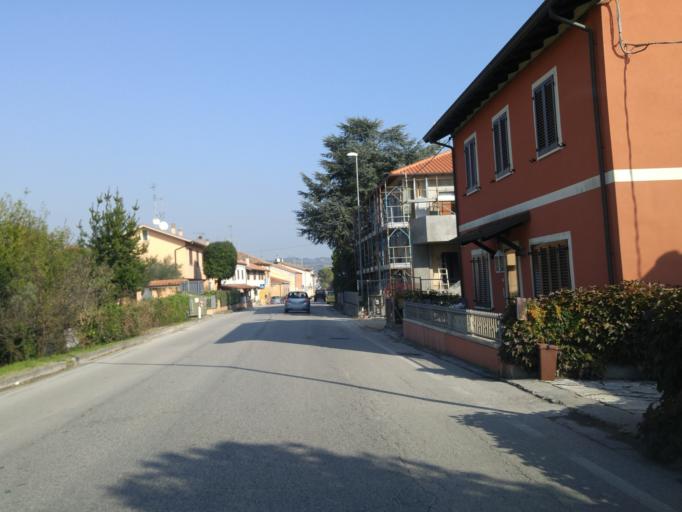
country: IT
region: The Marches
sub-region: Provincia di Pesaro e Urbino
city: Lucrezia
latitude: 43.7792
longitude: 12.9415
